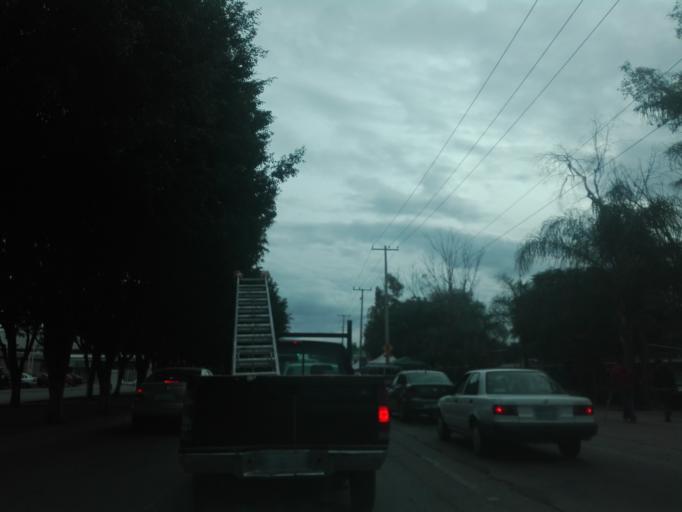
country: MX
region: Guanajuato
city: Leon
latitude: 21.1101
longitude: -101.6558
